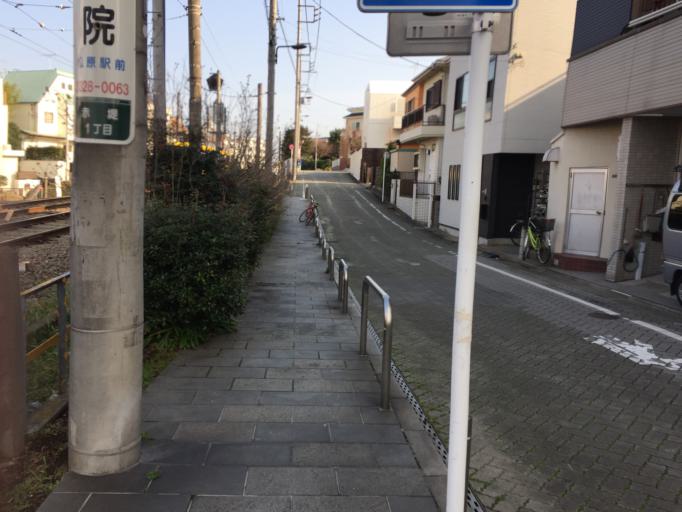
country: JP
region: Tokyo
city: Tokyo
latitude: 35.6570
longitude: 139.6438
